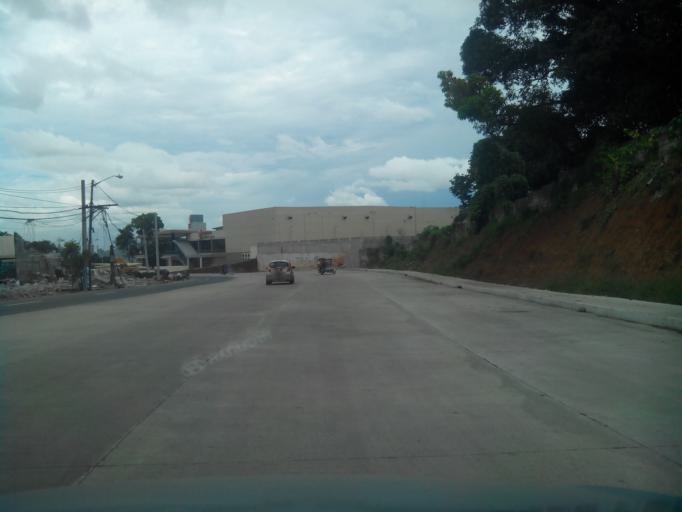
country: PH
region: Calabarzon
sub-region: Province of Rizal
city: Taytay
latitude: 14.5939
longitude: 121.1751
